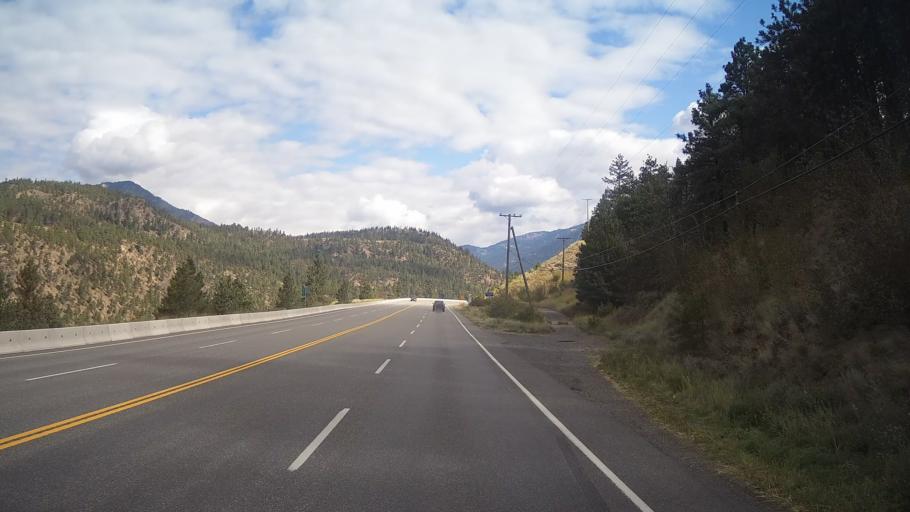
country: CA
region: British Columbia
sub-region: Thompson-Nicola Regional District
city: Ashcroft
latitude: 50.2415
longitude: -121.5730
